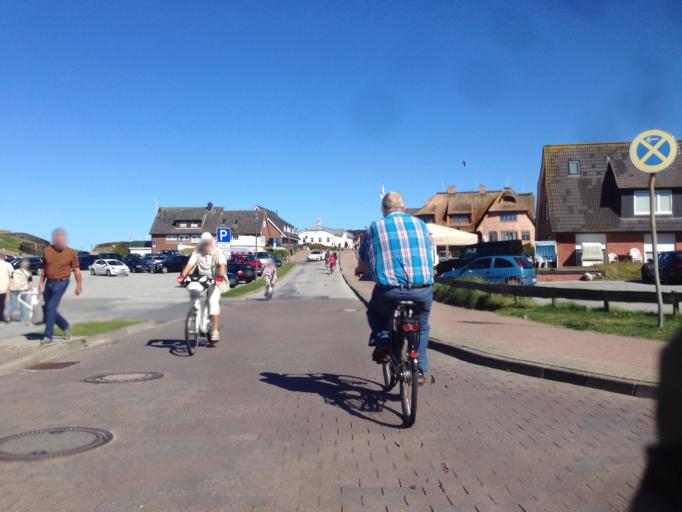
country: DE
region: Schleswig-Holstein
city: Westerland
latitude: 54.9349
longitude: 8.3164
